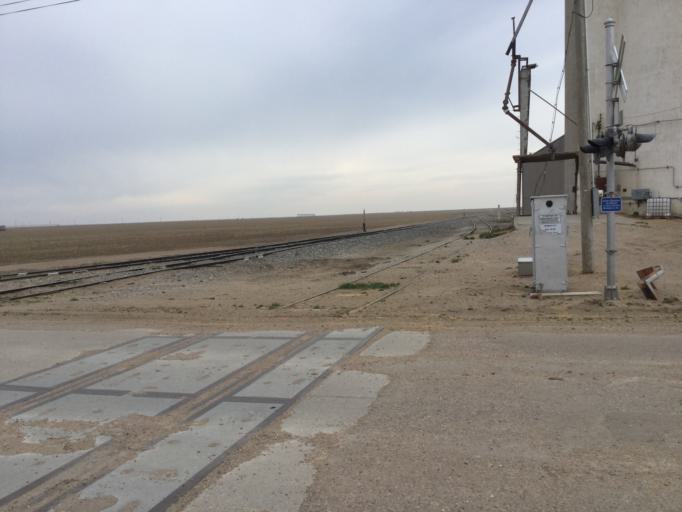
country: US
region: Kansas
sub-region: Stanton County
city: Johnson
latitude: 37.5624
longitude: -101.5629
